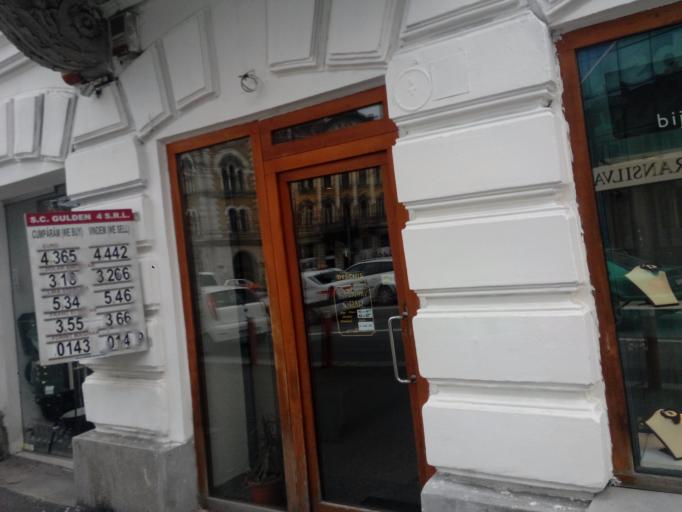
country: RO
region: Cluj
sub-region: Municipiul Cluj-Napoca
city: Cluj-Napoca
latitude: 46.7734
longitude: 23.5884
